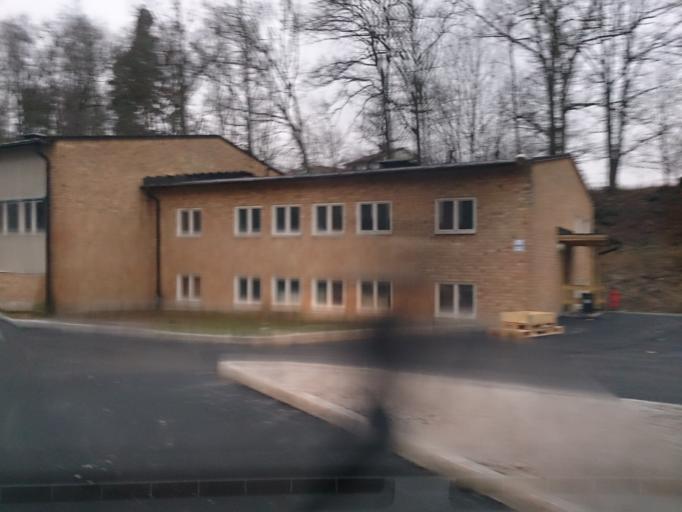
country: SE
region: OEstergoetland
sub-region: Atvidabergs Kommun
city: Atvidaberg
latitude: 58.2069
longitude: 16.0073
